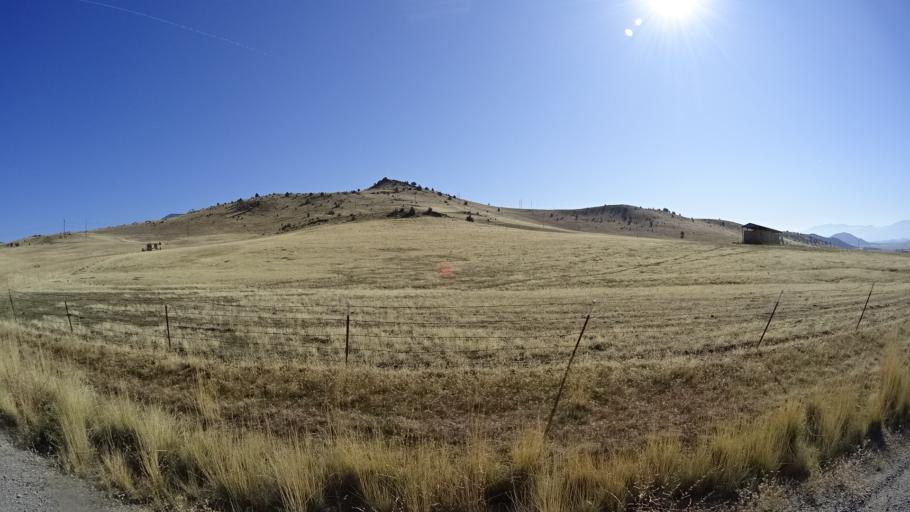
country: US
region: California
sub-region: Siskiyou County
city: Montague
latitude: 41.7459
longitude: -122.3633
